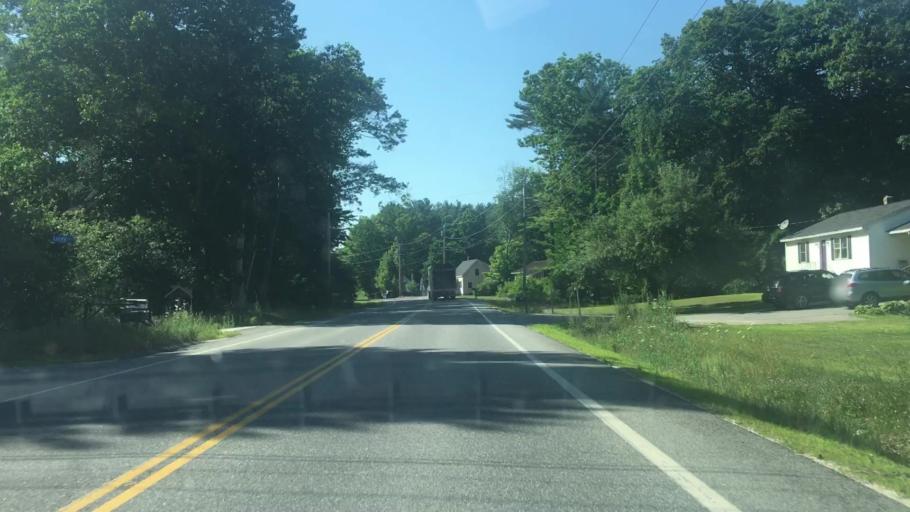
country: US
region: Maine
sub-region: York County
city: Buxton
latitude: 43.5880
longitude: -70.5201
